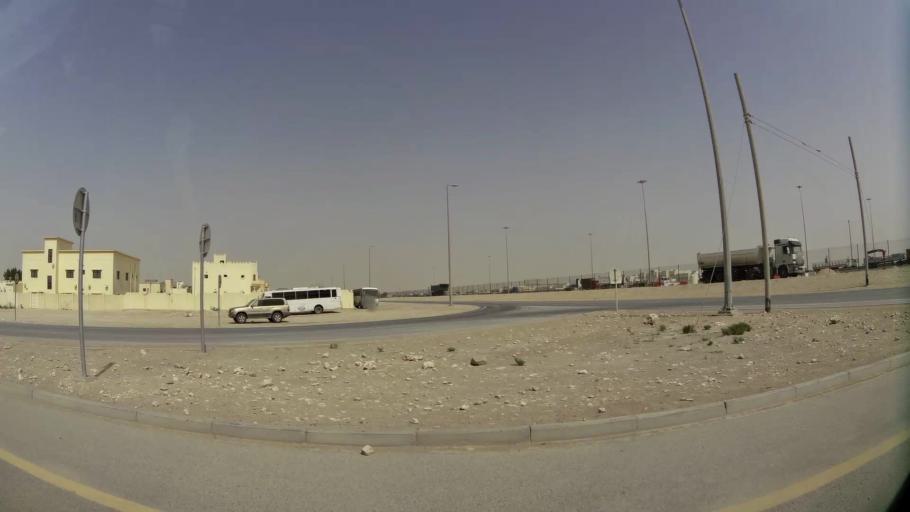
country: QA
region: Baladiyat ar Rayyan
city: Ar Rayyan
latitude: 25.1869
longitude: 51.3618
